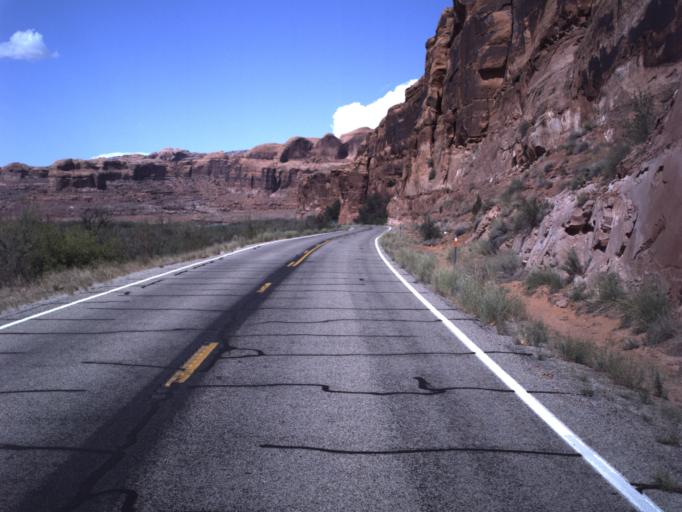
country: US
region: Utah
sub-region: Grand County
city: Moab
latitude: 38.5625
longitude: -109.6314
